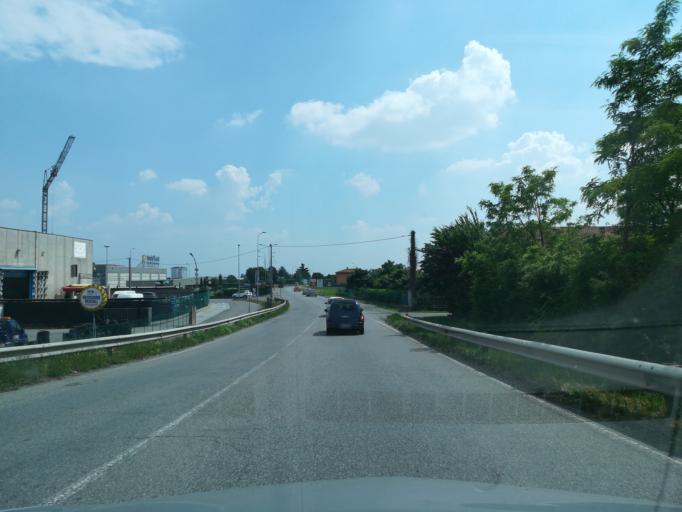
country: IT
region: Lombardy
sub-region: Provincia di Bergamo
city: Bolgare
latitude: 45.6426
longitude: 9.8079
